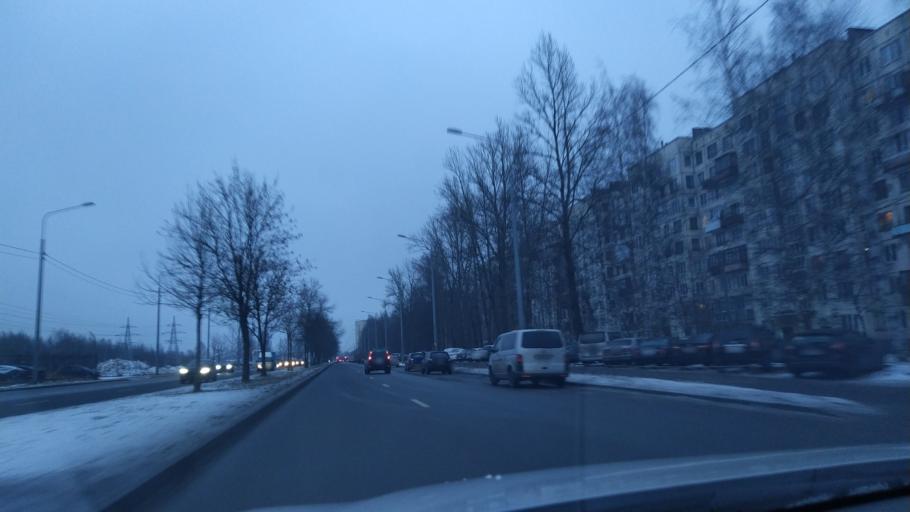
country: RU
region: St.-Petersburg
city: Grazhdanka
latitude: 60.0184
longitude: 30.4204
